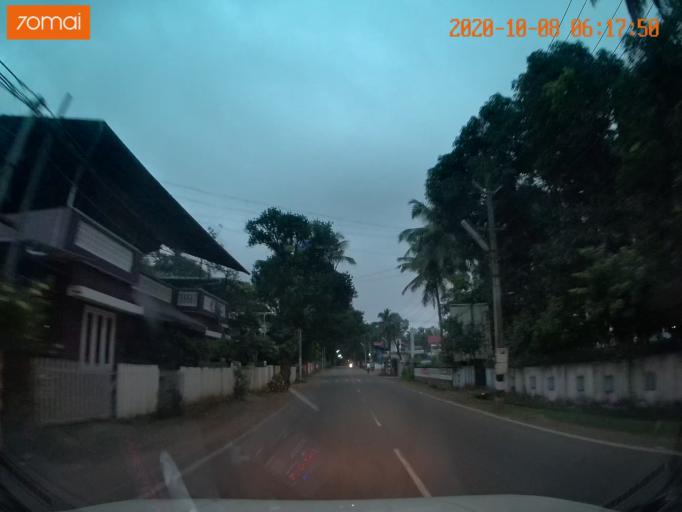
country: IN
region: Kerala
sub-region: Thrissur District
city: Trichur
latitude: 10.5125
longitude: 76.2538
